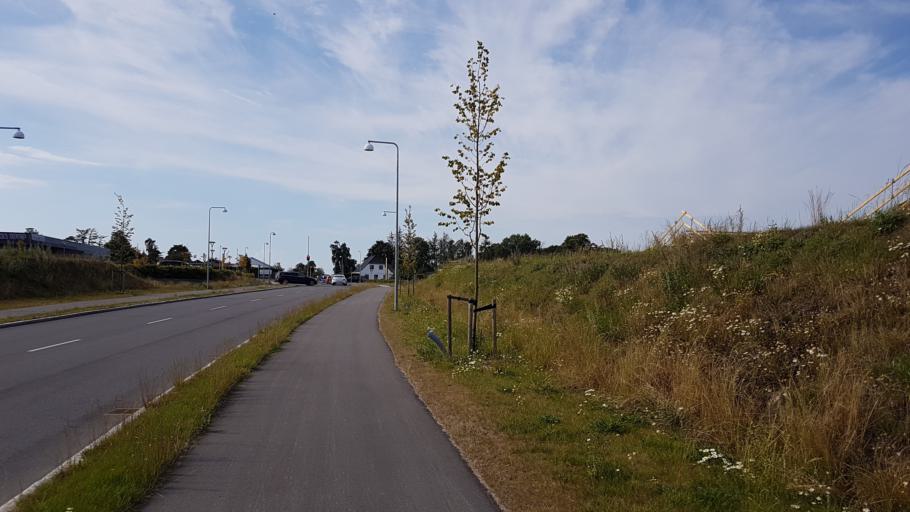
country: DK
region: Zealand
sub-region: Roskilde Kommune
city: Jyllinge
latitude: 55.7625
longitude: 12.1190
